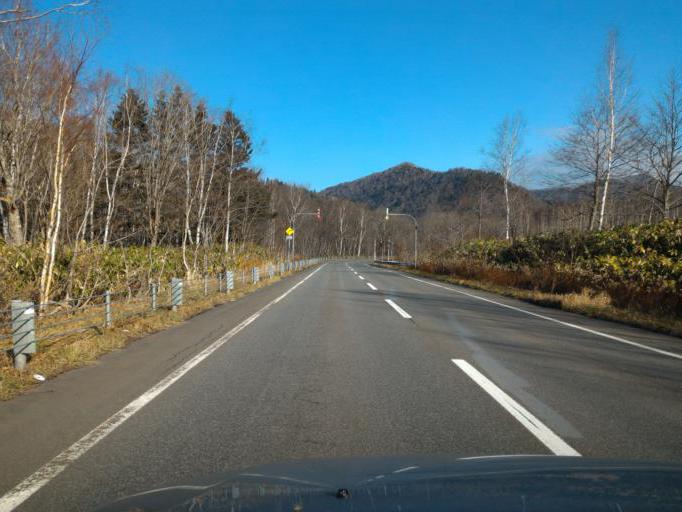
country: JP
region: Hokkaido
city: Ashibetsu
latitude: 43.3204
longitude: 142.1454
